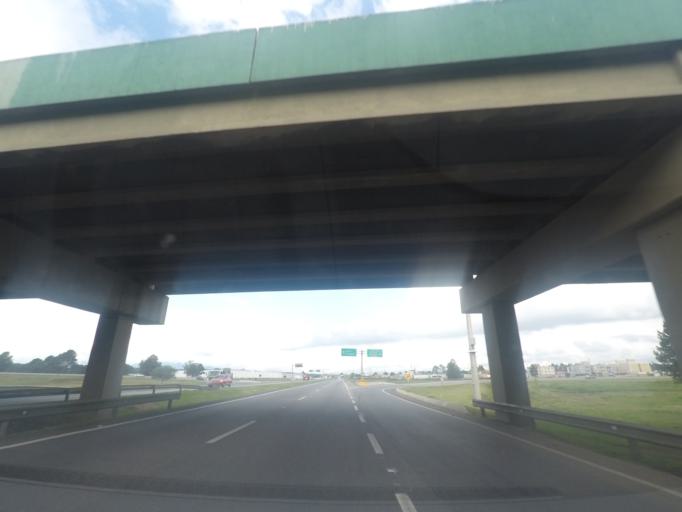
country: BR
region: Parana
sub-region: Sao Jose Dos Pinhais
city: Sao Jose dos Pinhais
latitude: -25.5116
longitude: -49.1281
